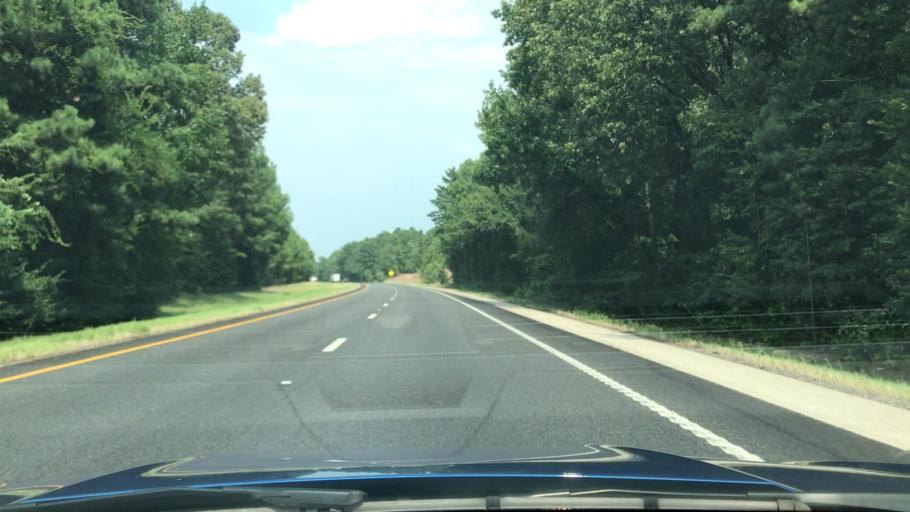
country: US
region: Texas
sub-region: Gregg County
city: Longview
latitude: 32.4308
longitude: -94.7651
